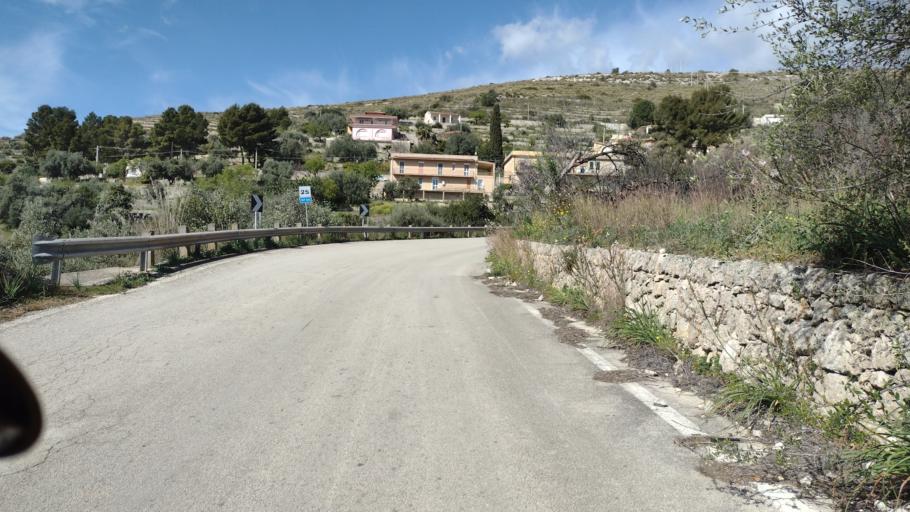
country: IT
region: Sicily
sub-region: Provincia di Siracusa
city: Noto
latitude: 36.9075
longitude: 15.0275
